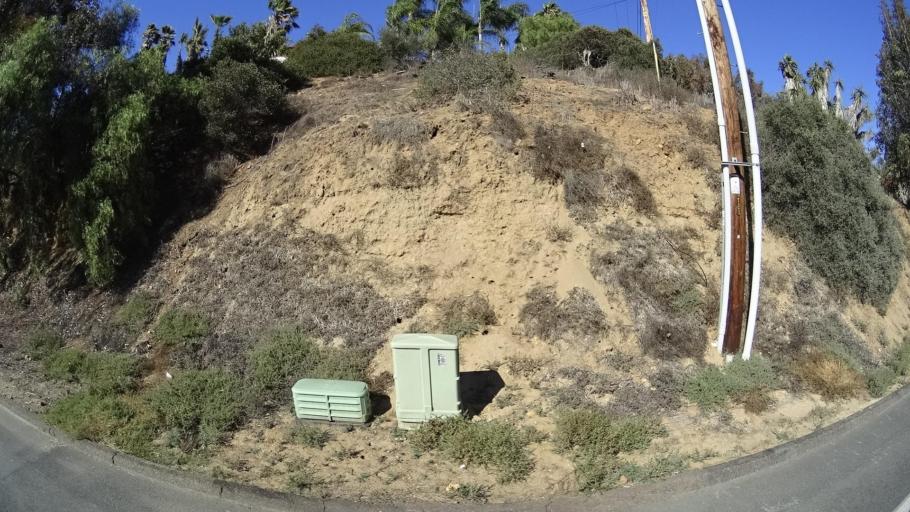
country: US
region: California
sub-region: San Diego County
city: Bonita
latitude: 32.6654
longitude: -117.0362
